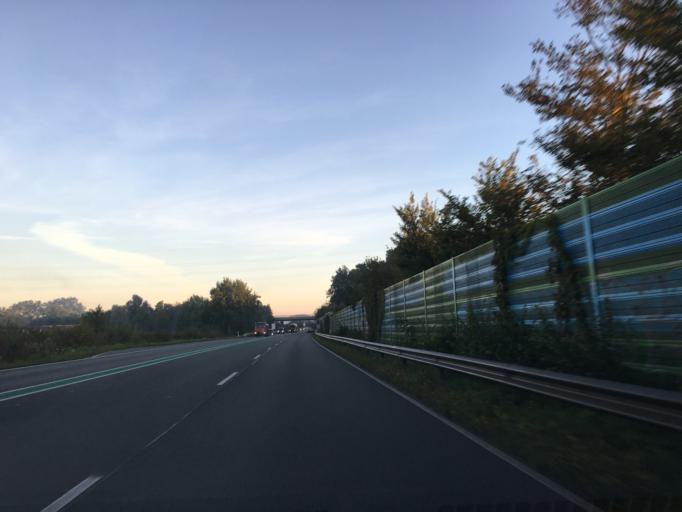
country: DE
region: North Rhine-Westphalia
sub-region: Regierungsbezirk Munster
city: Steinfurt
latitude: 52.1188
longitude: 7.3699
